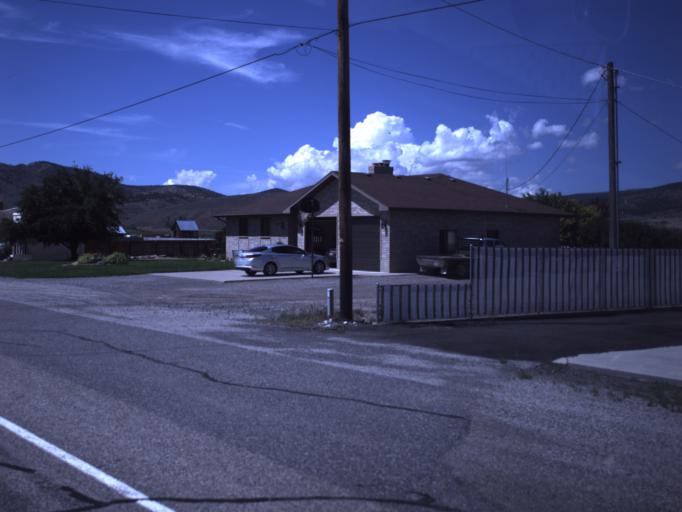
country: US
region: Utah
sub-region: Piute County
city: Junction
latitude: 38.1664
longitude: -112.2796
